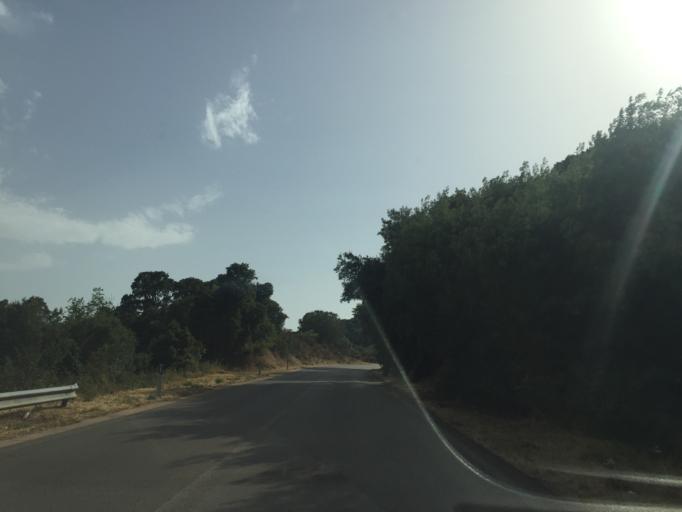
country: IT
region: Sardinia
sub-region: Provincia di Olbia-Tempio
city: Luras
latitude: 40.9344
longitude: 9.1856
